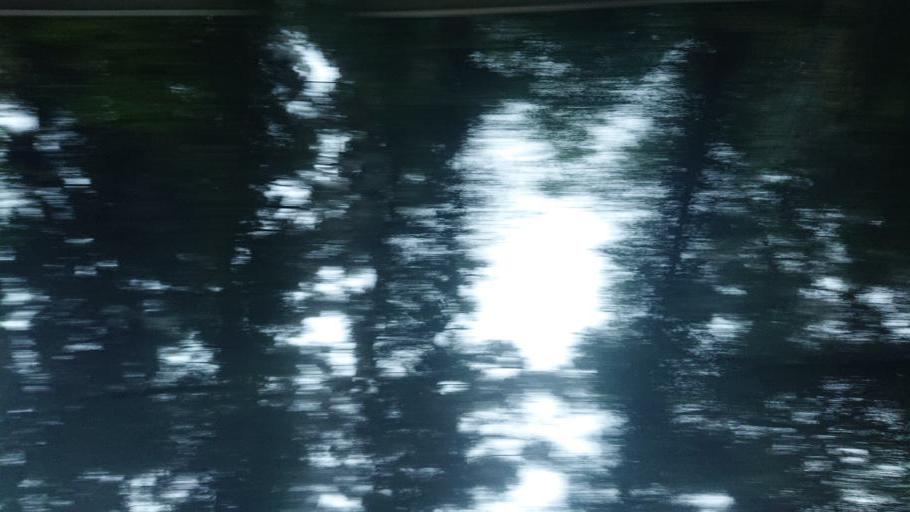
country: TW
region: Taiwan
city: Lugu
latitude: 23.5060
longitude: 120.7026
